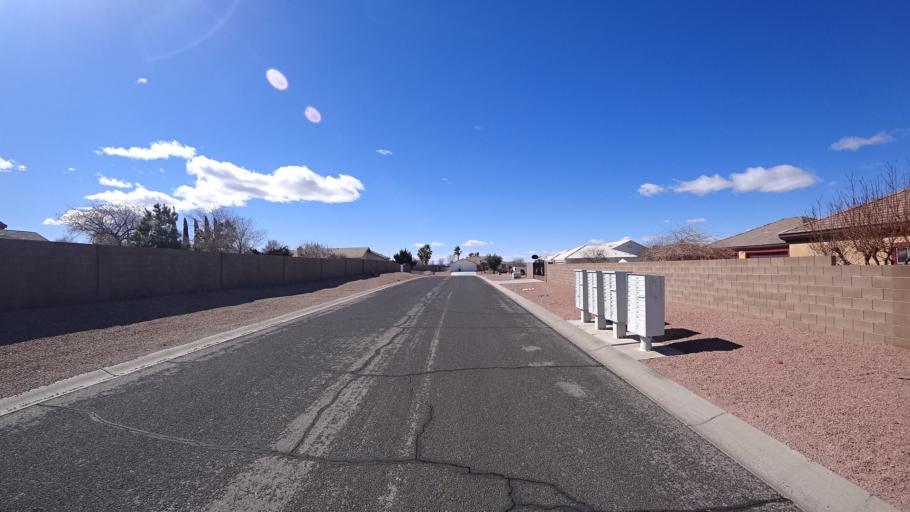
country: US
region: Arizona
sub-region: Mohave County
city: Kingman
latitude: 35.2073
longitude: -113.9740
